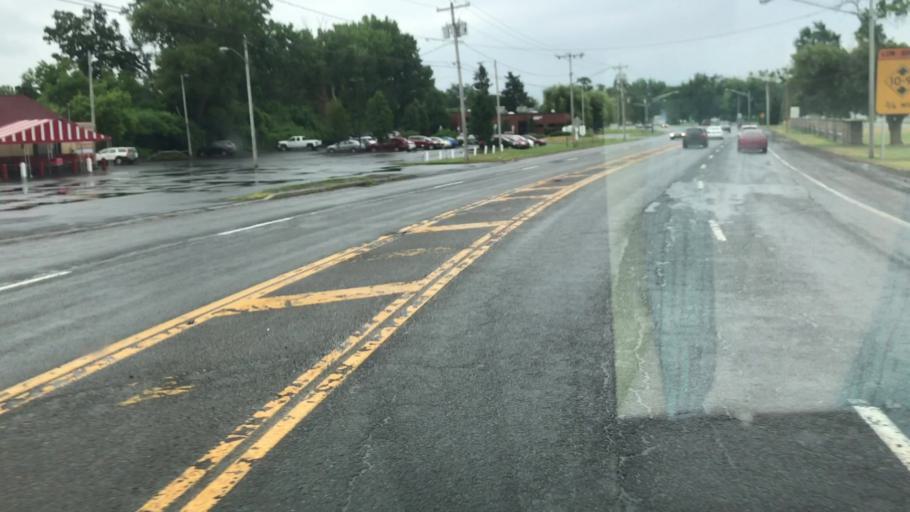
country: US
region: New York
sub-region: Onondaga County
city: Liverpool
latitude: 43.1009
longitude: -76.2024
